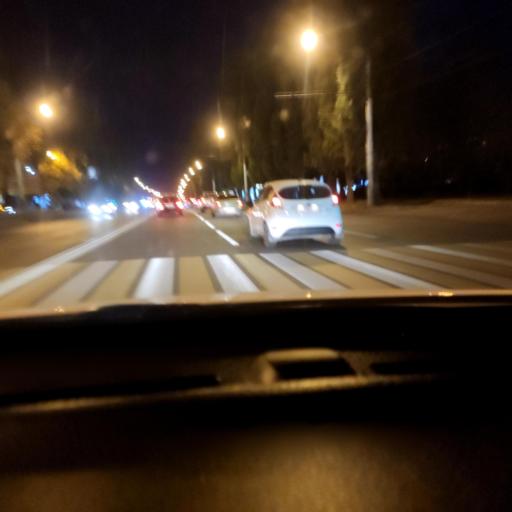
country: RU
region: Voronezj
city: Maslovka
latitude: 51.6165
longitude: 39.2372
